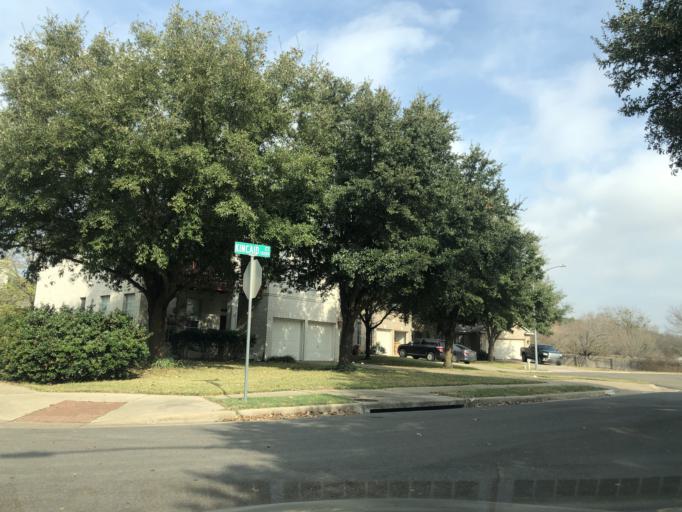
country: US
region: Texas
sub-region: Travis County
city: Wells Branch
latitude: 30.4195
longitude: -97.6797
